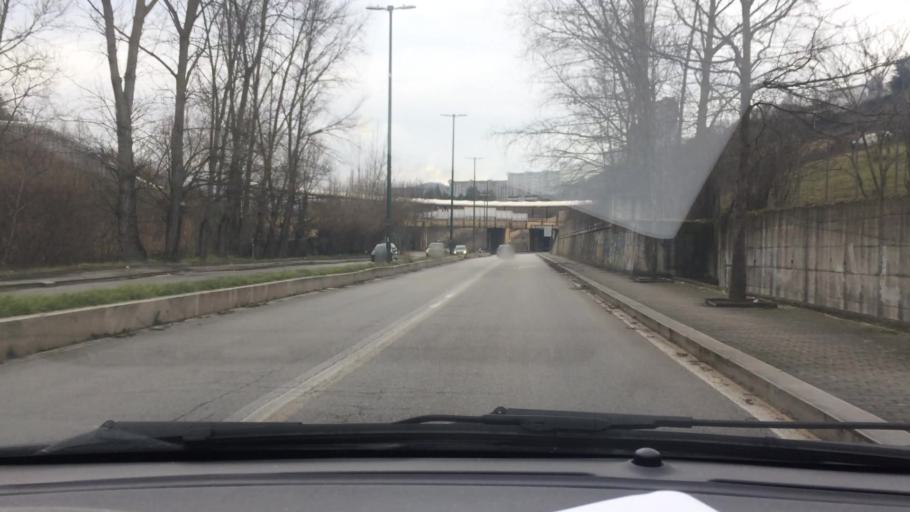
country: IT
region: Basilicate
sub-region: Provincia di Potenza
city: Potenza
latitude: 40.6385
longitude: 15.7963
